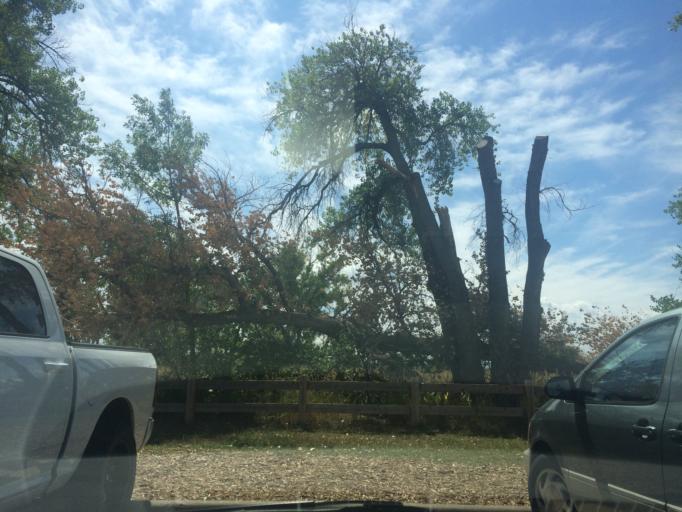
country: US
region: Colorado
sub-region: Adams County
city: Northglenn
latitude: 39.9573
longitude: -105.0117
